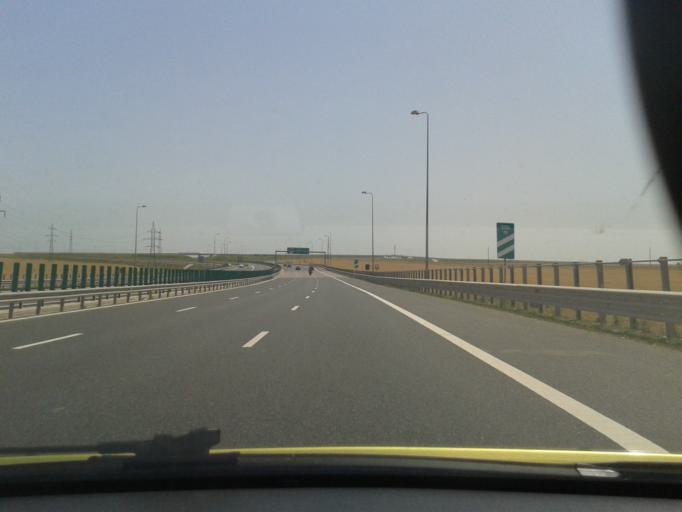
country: RO
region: Constanta
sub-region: Comuna Cumpana
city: Cumpana
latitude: 44.1579
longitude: 28.5505
